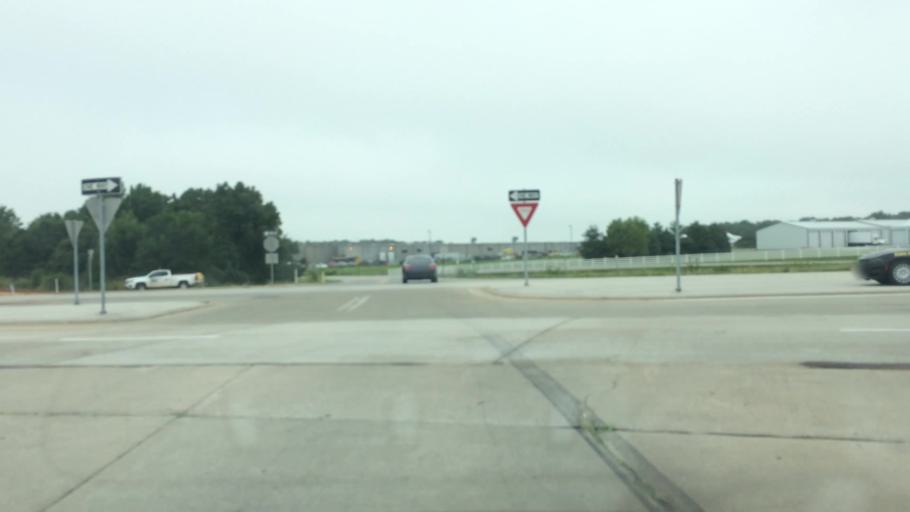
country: US
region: Missouri
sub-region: Greene County
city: Strafford
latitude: 37.2727
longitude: -93.2142
